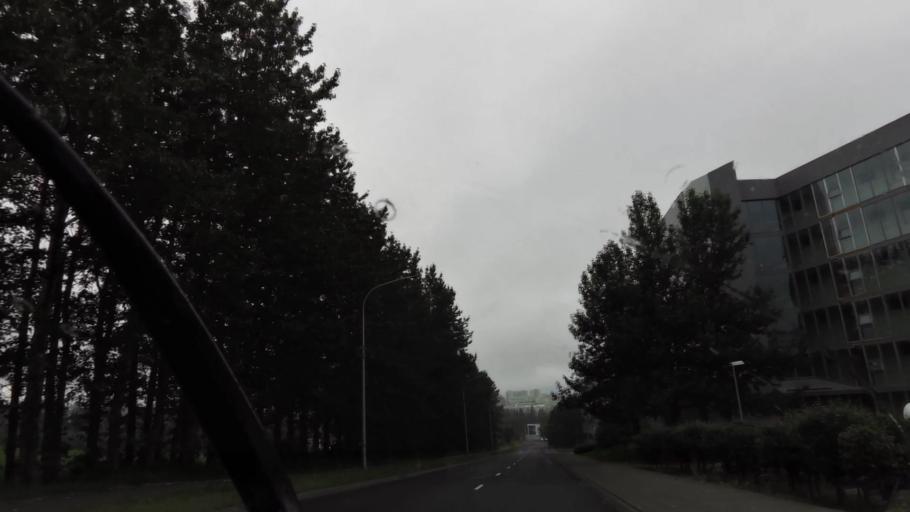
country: IS
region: Capital Region
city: Reykjavik
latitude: 64.1226
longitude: -21.8922
